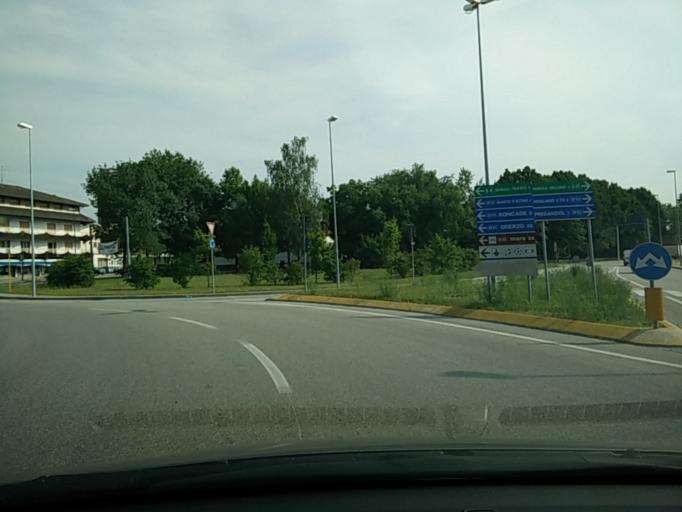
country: IT
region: Veneto
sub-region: Provincia di Treviso
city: Casale sul Sile
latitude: 45.5999
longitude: 12.3255
